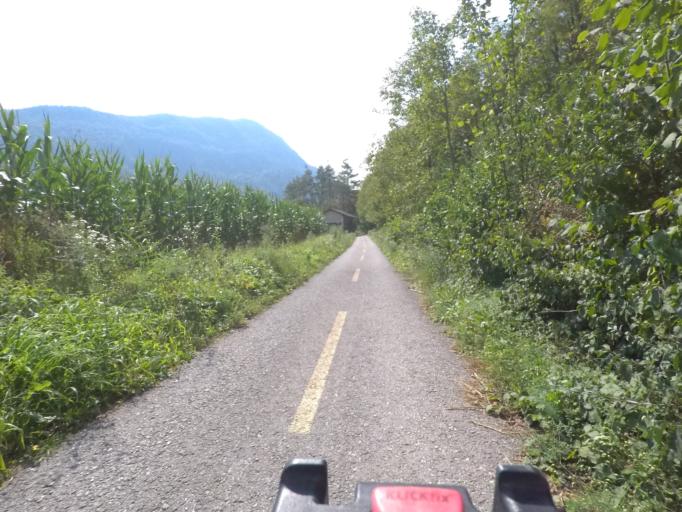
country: IT
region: Friuli Venezia Giulia
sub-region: Provincia di Udine
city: Zuglio
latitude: 46.4352
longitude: 13.0246
